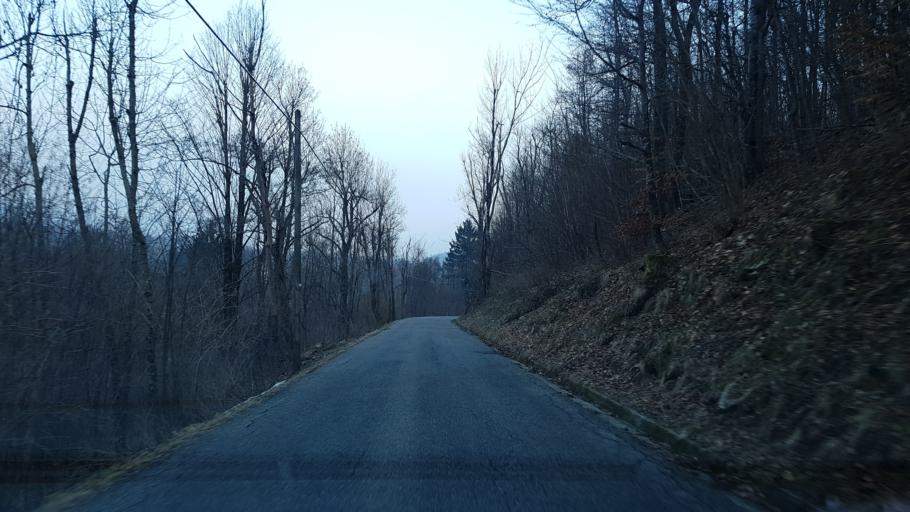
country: IT
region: Friuli Venezia Giulia
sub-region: Provincia di Udine
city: Taipana
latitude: 46.2569
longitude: 13.3598
